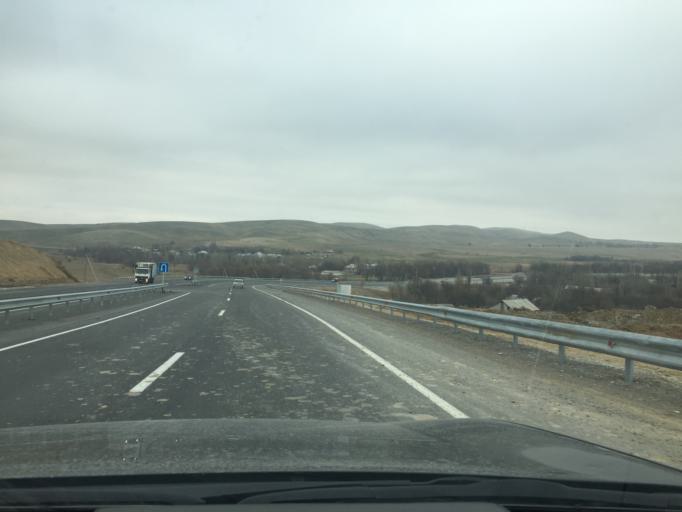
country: KZ
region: Ongtustik Qazaqstan
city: Sastobe
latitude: 42.4957
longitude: 69.9596
